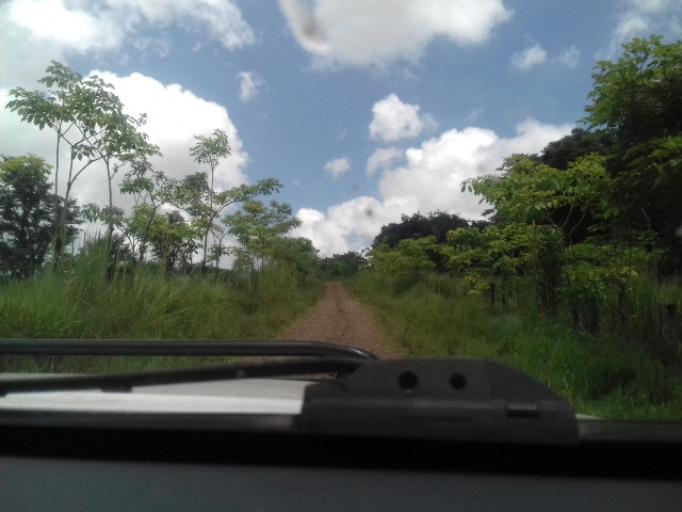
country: NI
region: Matagalpa
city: Rio Blanco
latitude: 12.9990
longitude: -85.3868
